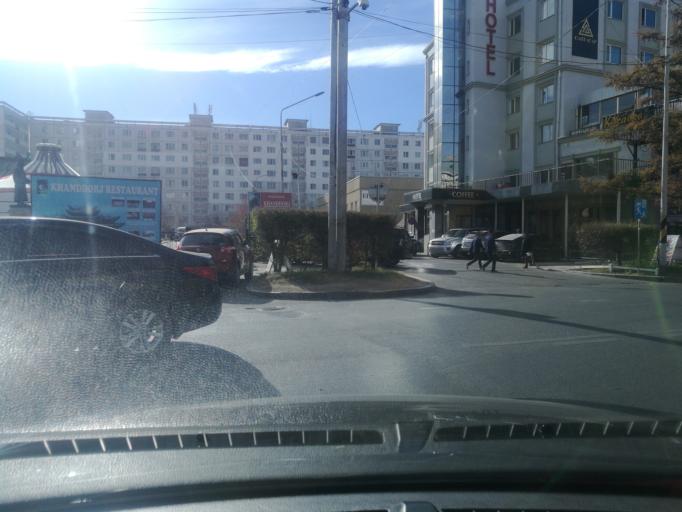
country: MN
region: Ulaanbaatar
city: Ulaanbaatar
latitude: 47.9146
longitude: 106.9090
